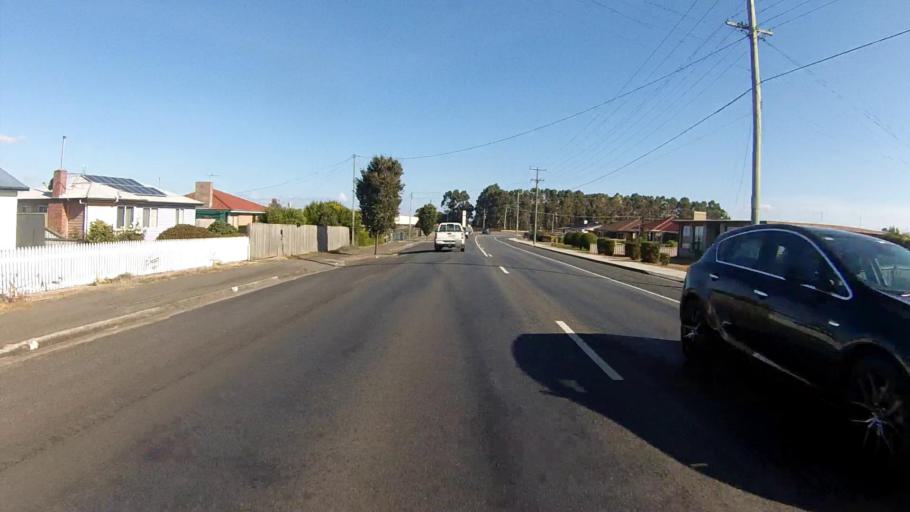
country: AU
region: Tasmania
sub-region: Sorell
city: Sorell
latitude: -42.7886
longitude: 147.5615
